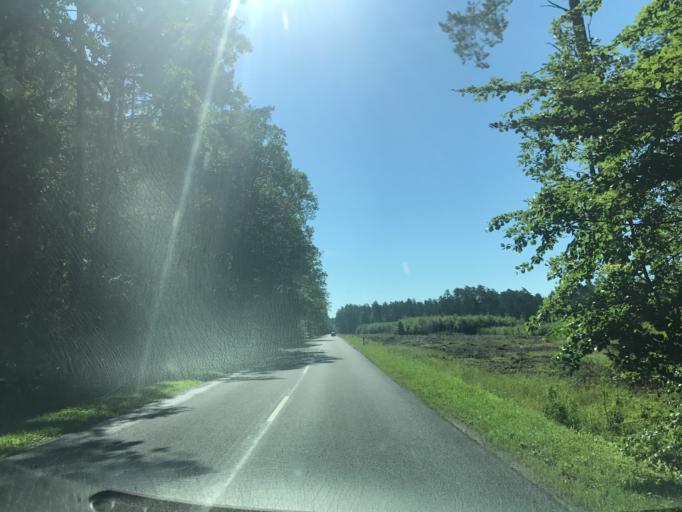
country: PL
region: Pomeranian Voivodeship
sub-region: Powiat slupski
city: Potegowo
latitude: 54.4037
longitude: 17.4531
